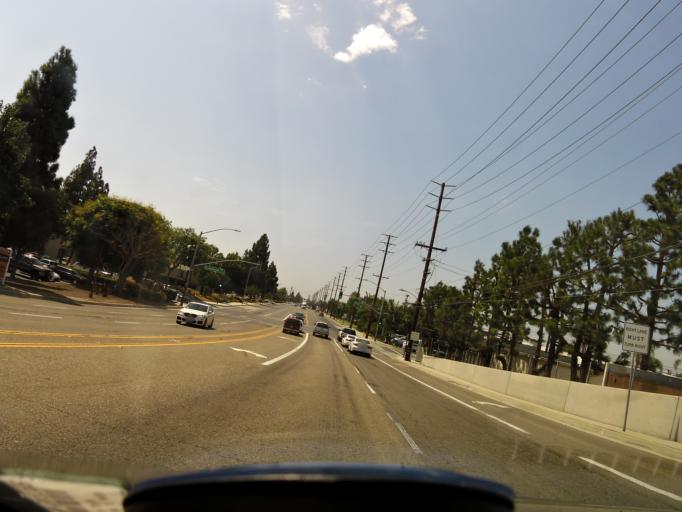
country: US
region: California
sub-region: Orange County
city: Tustin
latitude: 33.7159
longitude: -117.8462
